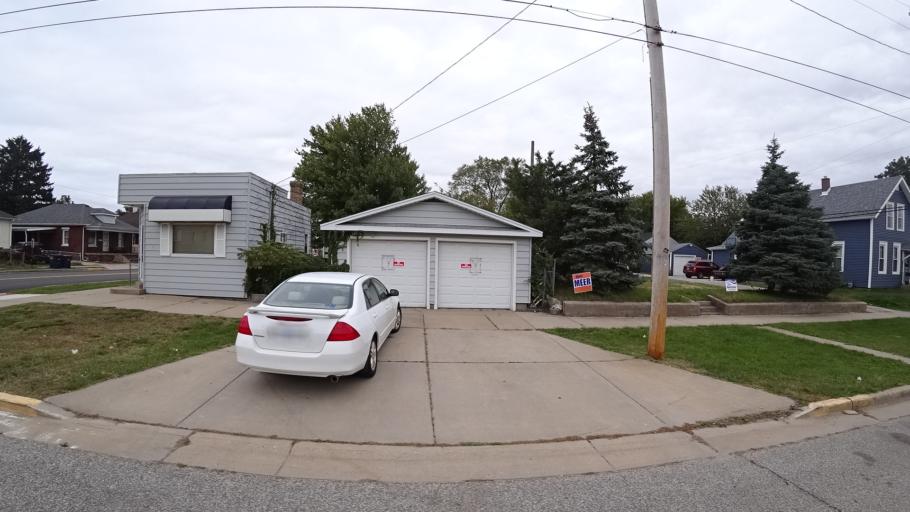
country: US
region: Indiana
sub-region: LaPorte County
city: Michigan City
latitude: 41.7050
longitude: -86.8973
